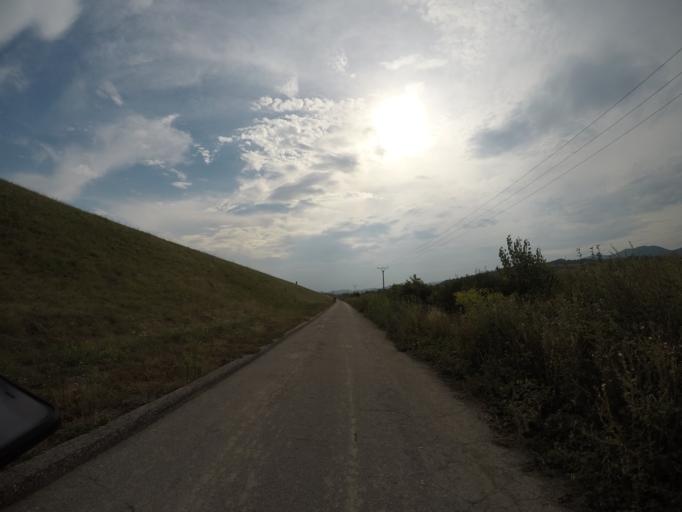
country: SK
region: Trenciansky
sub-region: Okres Trencin
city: Trencin
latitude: 48.8815
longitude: 17.9930
